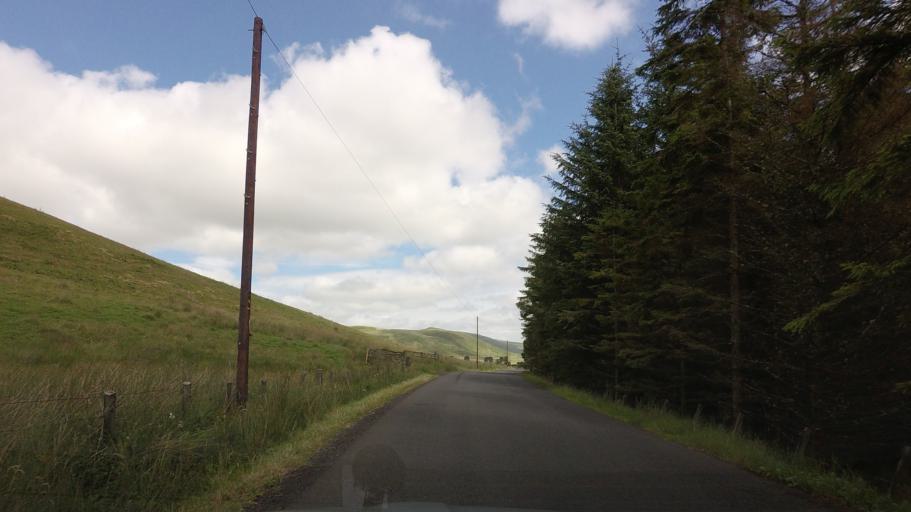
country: GB
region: Scotland
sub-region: The Scottish Borders
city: Innerleithen
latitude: 55.4424
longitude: -3.1062
